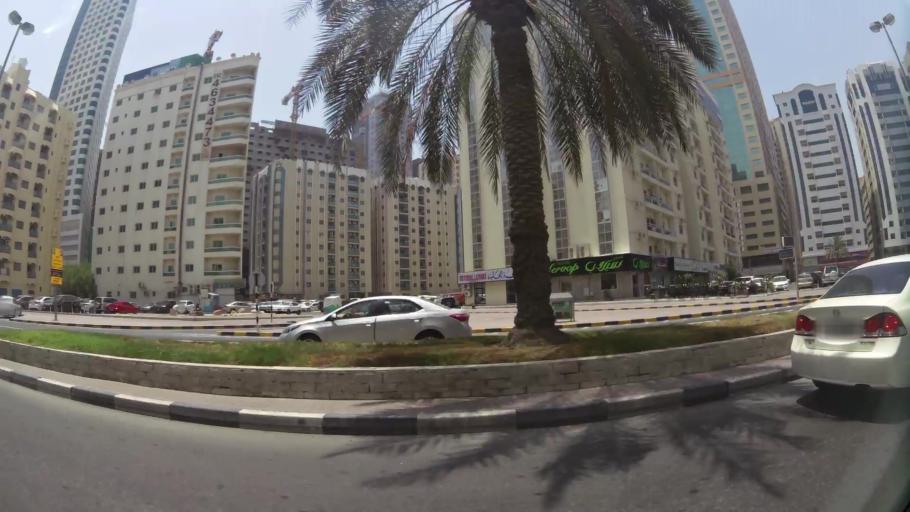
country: AE
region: Ash Shariqah
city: Sharjah
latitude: 25.3206
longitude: 55.3858
